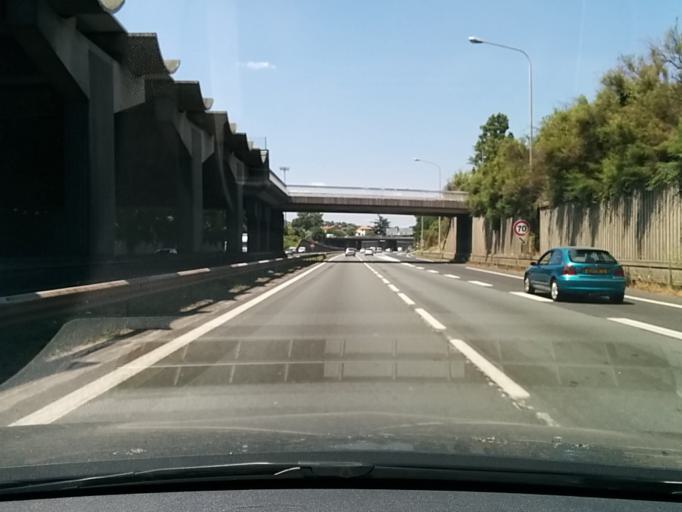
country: FR
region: Midi-Pyrenees
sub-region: Departement de la Haute-Garonne
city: Ramonville-Saint-Agne
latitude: 43.5723
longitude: 1.4568
